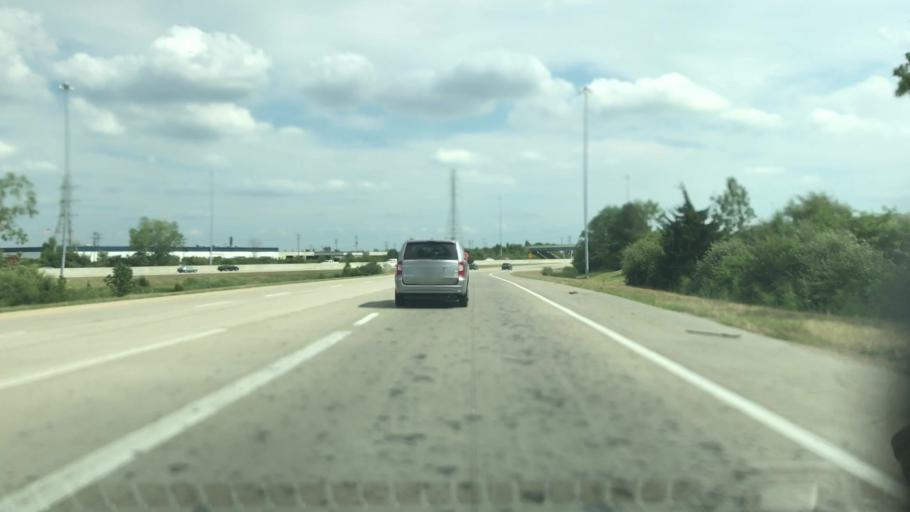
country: US
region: Ohio
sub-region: Franklin County
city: Lincoln Village
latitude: 39.9743
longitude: -83.1208
